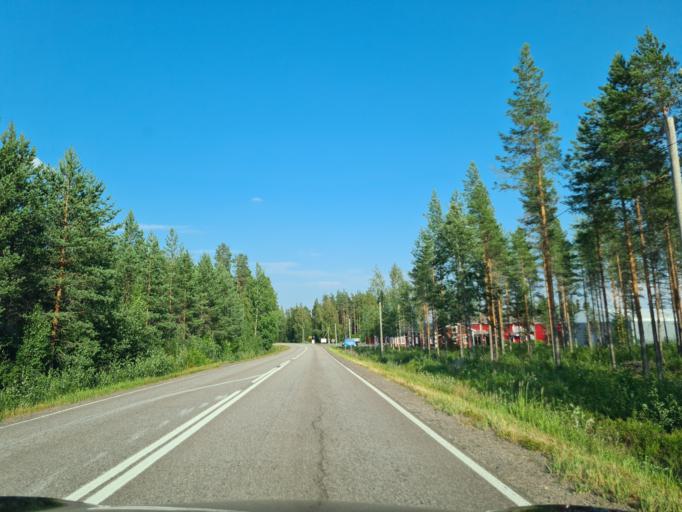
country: FI
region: Satakunta
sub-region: Pohjois-Satakunta
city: Karvia
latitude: 62.3258
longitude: 22.6955
